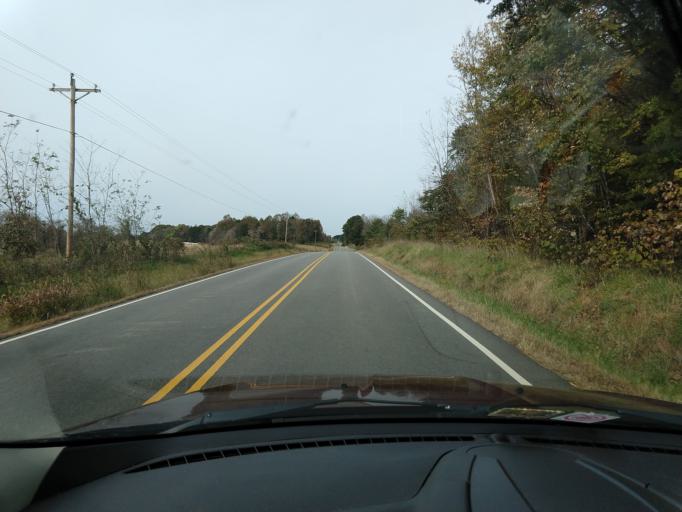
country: US
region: Virginia
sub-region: Franklin County
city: Union Hall
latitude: 36.9593
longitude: -79.5699
